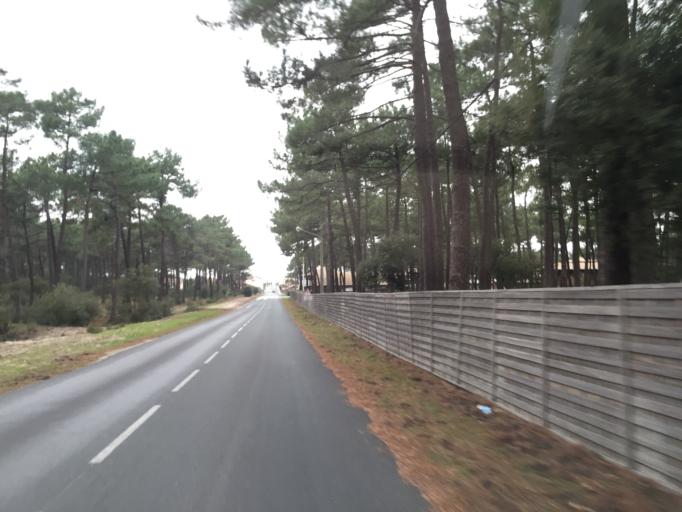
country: FR
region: Aquitaine
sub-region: Departement de la Gironde
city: Hourtin
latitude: 45.2226
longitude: -1.1625
